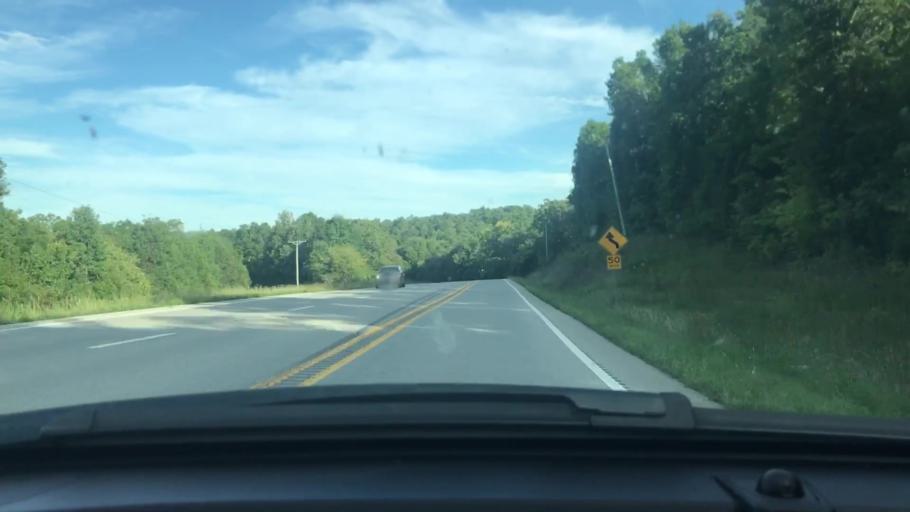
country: US
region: Arkansas
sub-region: Sharp County
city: Cherokee Village
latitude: 36.2744
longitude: -91.3580
